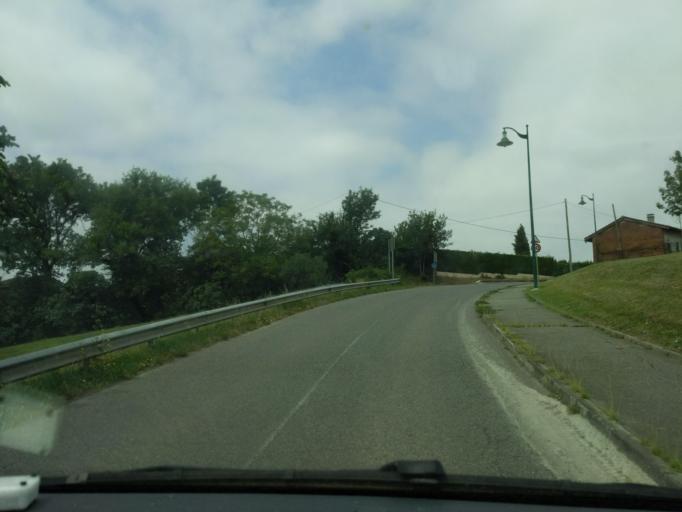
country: FR
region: Midi-Pyrenees
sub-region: Departement de la Haute-Garonne
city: Escalquens
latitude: 43.5215
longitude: 1.5617
